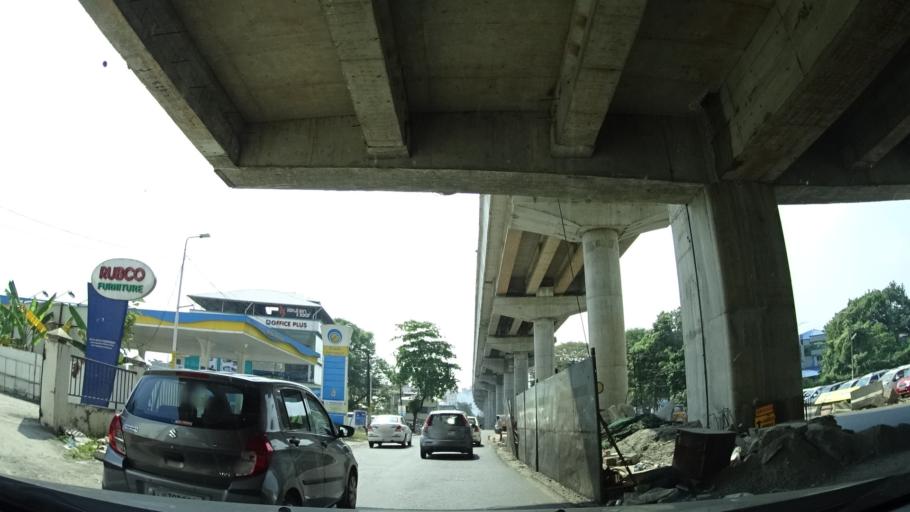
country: IN
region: Kerala
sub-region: Ernakulam
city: Elur
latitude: 10.0359
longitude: 76.3144
